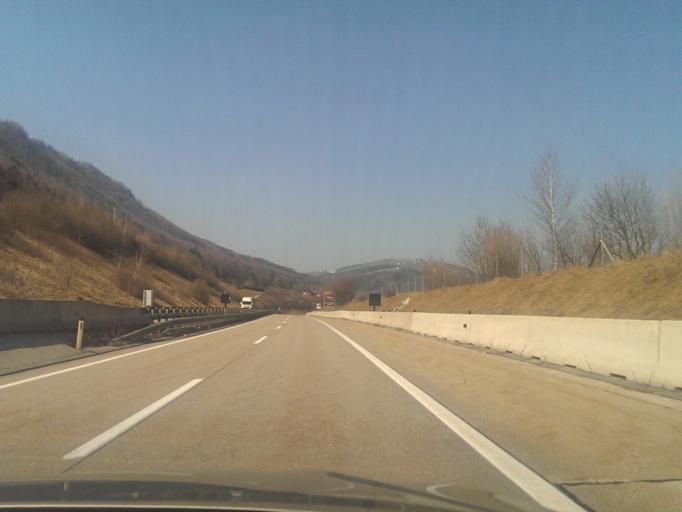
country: AT
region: Upper Austria
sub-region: Politischer Bezirk Kirchdorf an der Krems
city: Micheldorf in Oberoesterreich
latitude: 47.8713
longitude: 14.1214
